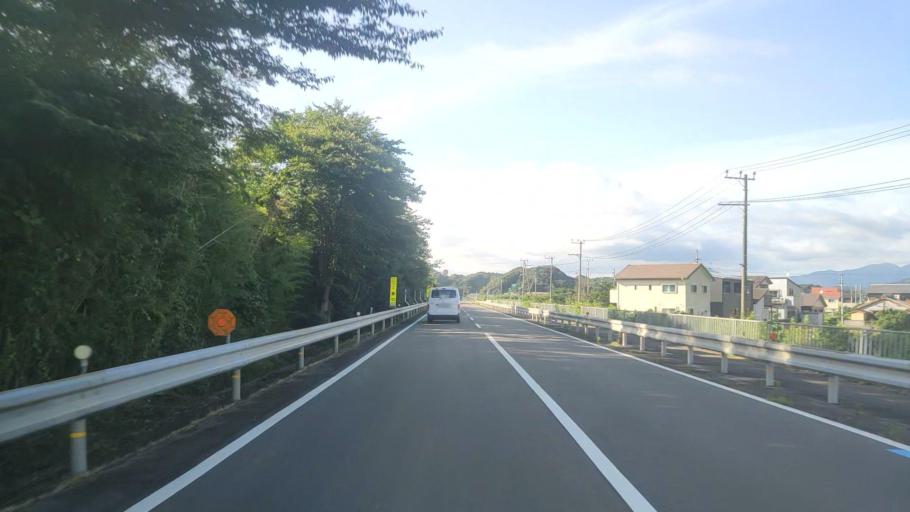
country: JP
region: Wakayama
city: Tanabe
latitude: 33.6748
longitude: 135.4078
